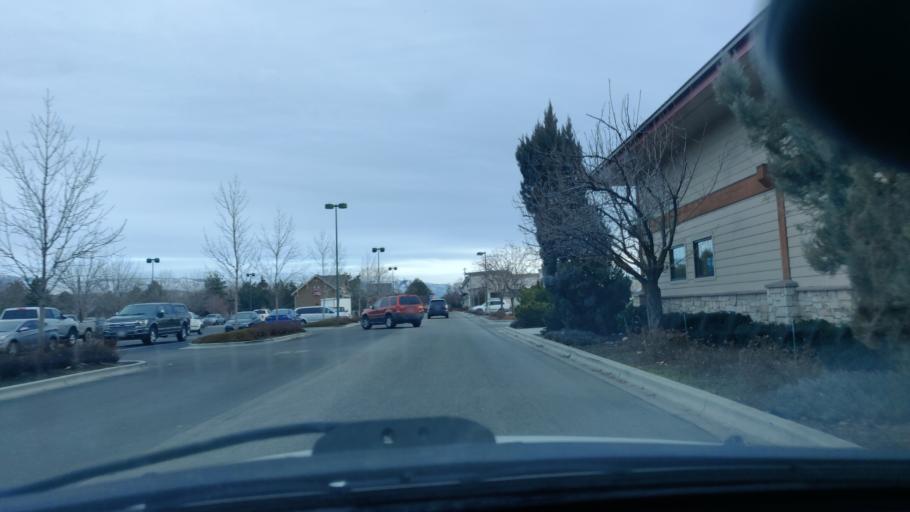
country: US
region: Idaho
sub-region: Ada County
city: Eagle
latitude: 43.6846
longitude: -116.3164
